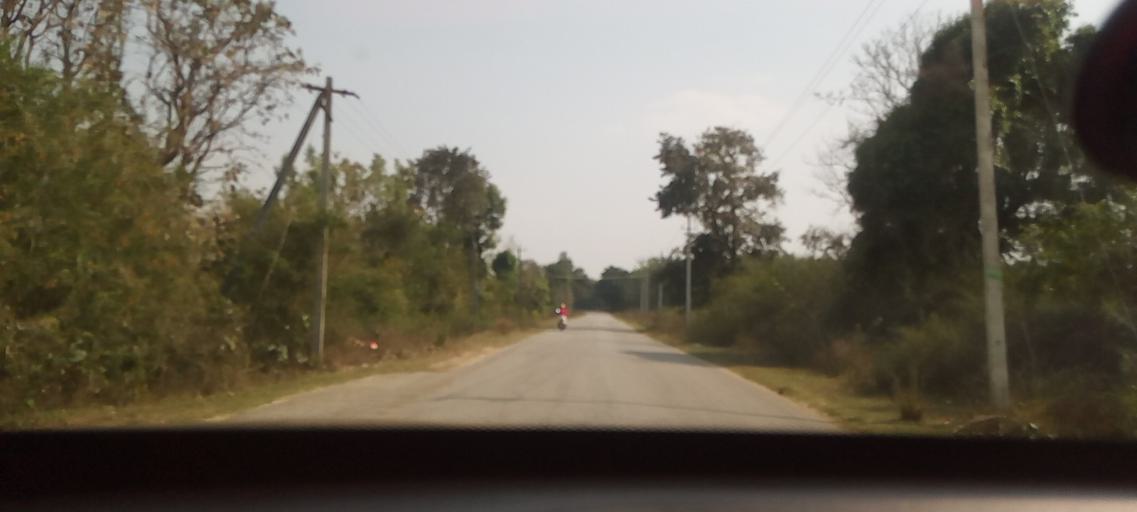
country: IN
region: Karnataka
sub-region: Hassan
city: Belur
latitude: 13.1773
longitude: 75.8107
